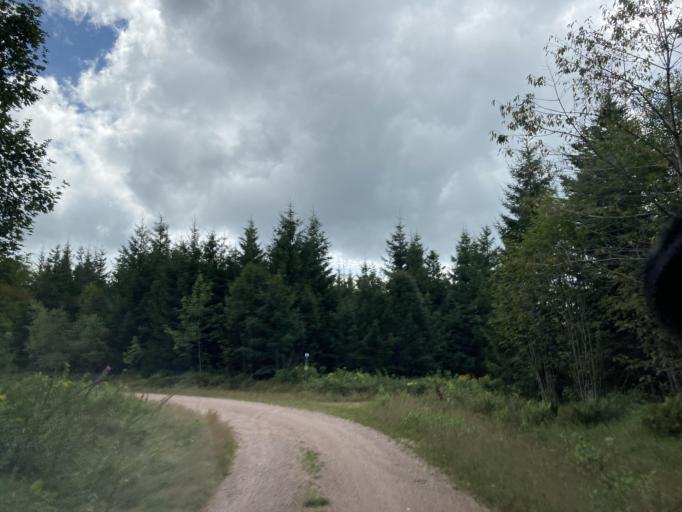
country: DE
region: Baden-Wuerttemberg
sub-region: Freiburg Region
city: Schonach im Schwarzwald
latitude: 48.1537
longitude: 8.1404
